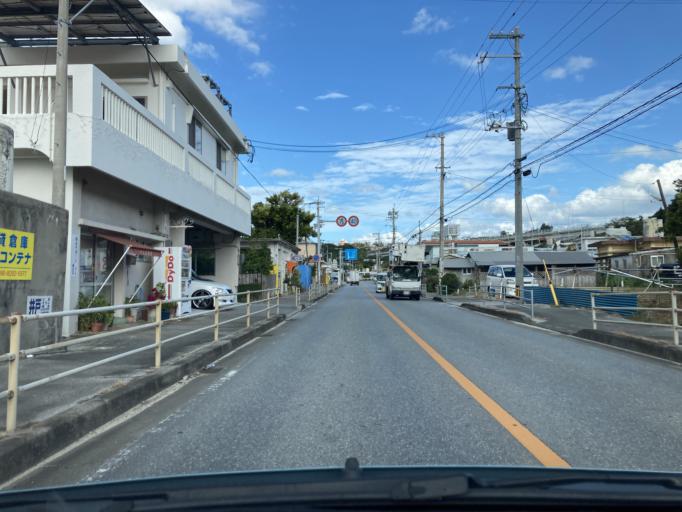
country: JP
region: Okinawa
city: Ishikawa
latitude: 26.4377
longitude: 127.8009
